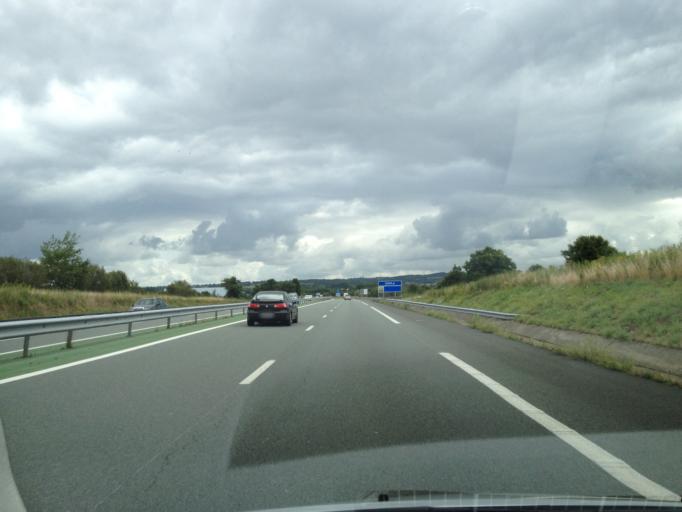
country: FR
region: Pays de la Loire
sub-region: Departement de la Vendee
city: Beaurepaire
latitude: 46.8960
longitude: -1.0787
